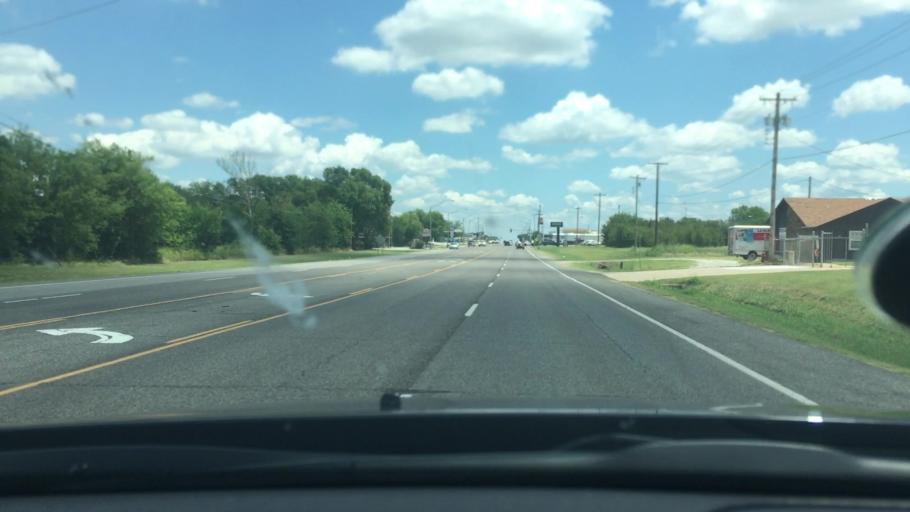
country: US
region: Oklahoma
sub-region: Carter County
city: Lone Grove
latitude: 34.1729
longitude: -97.2686
